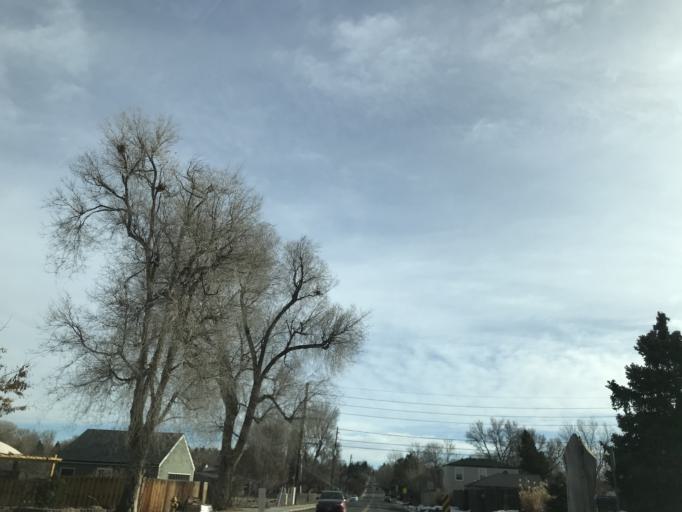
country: US
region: Colorado
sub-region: Arapahoe County
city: Littleton
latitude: 39.6024
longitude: -105.0095
